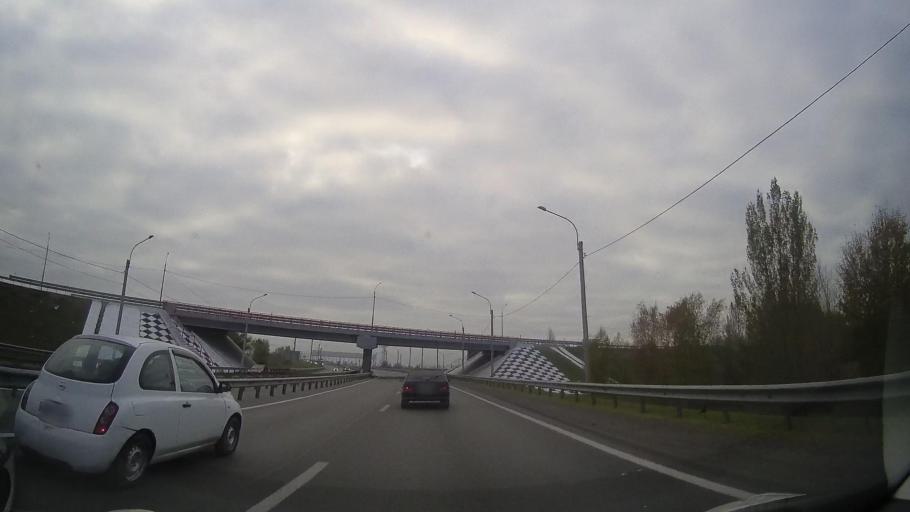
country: RU
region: Rostov
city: Bataysk
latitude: 47.1698
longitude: 39.7470
